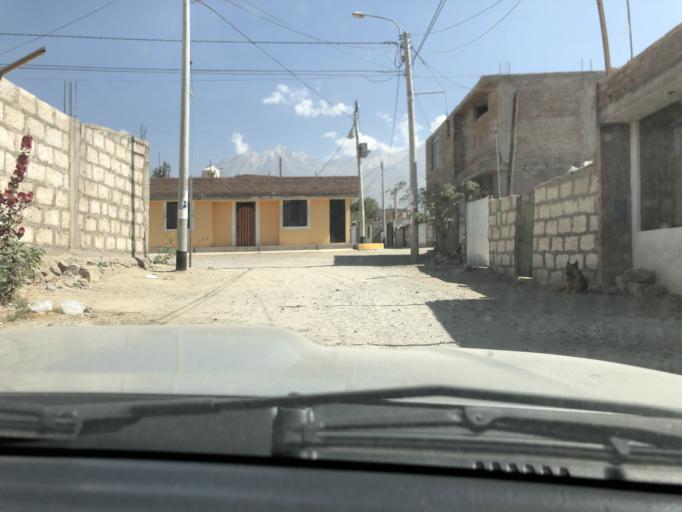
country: PE
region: Arequipa
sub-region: Provincia de Arequipa
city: Arequipa
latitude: -16.3408
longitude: -71.5504
